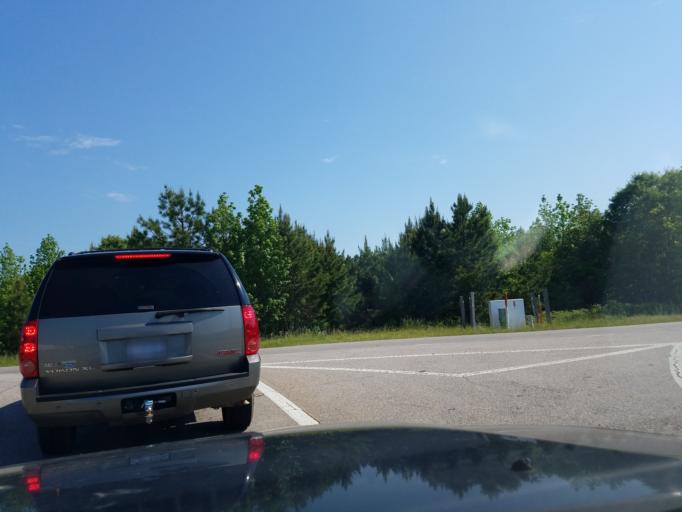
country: US
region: North Carolina
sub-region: Vance County
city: Henderson
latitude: 36.3385
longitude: -78.4452
